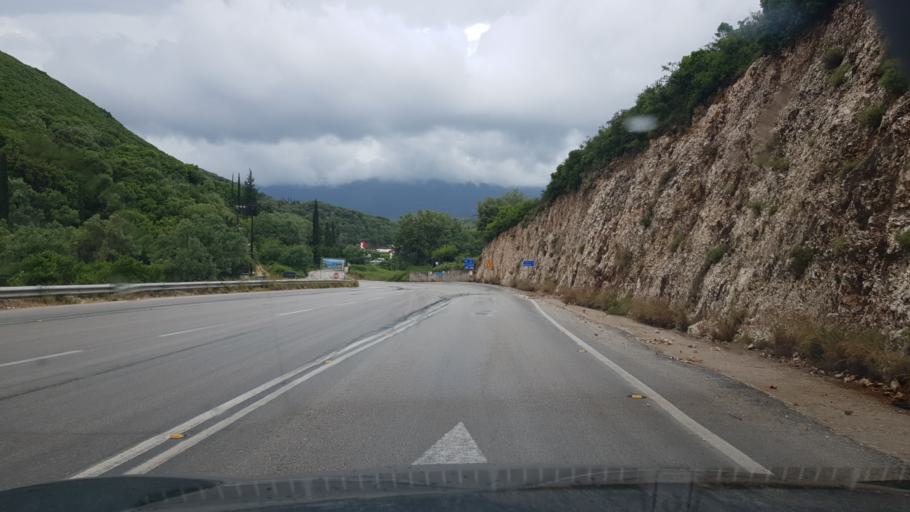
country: GR
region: Ionian Islands
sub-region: Lefkada
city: Nidri
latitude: 38.6330
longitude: 20.6669
